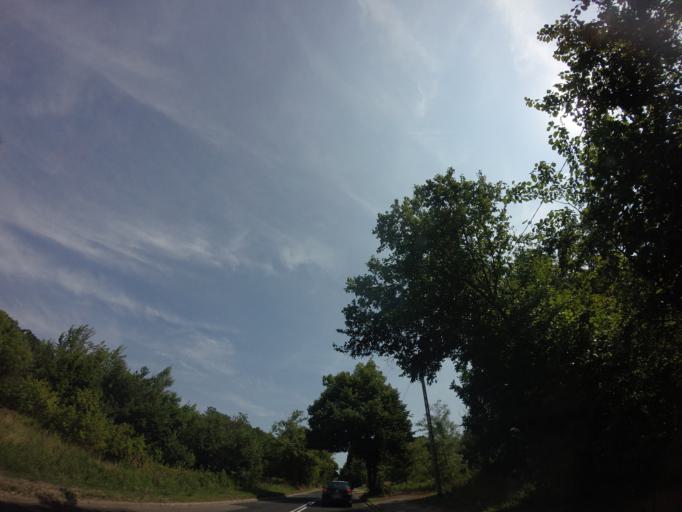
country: PL
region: West Pomeranian Voivodeship
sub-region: Szczecin
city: Szczecin
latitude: 53.3675
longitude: 14.6061
